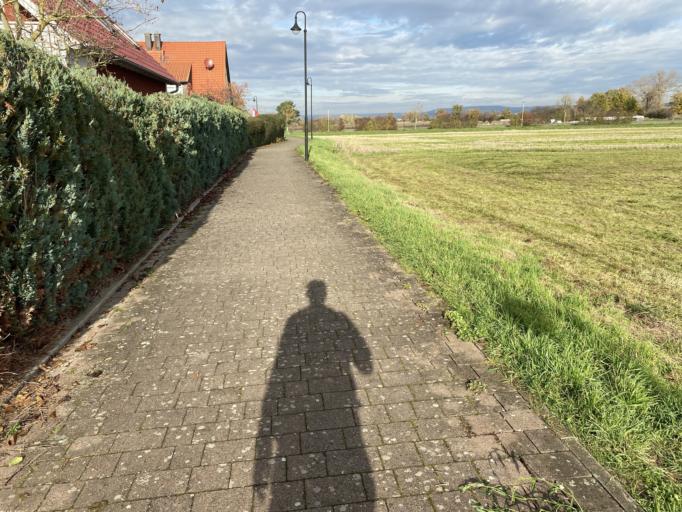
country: DE
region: Bavaria
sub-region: Regierungsbezirk Mittelfranken
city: Baiersdorf
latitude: 49.6556
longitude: 11.0450
